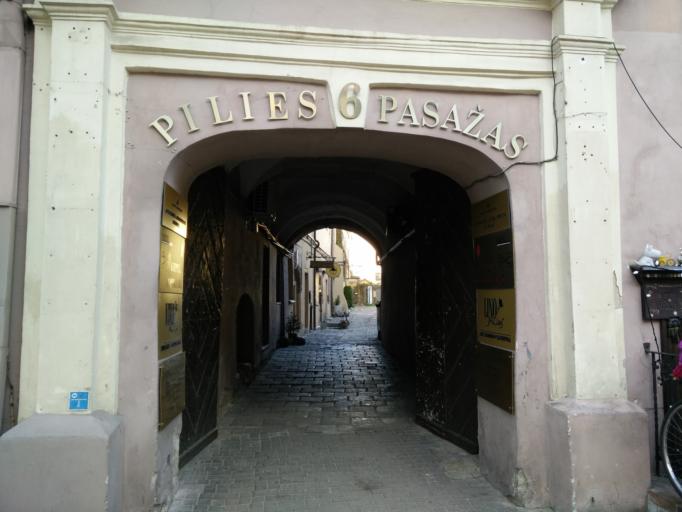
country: LT
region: Vilnius County
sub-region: Vilnius
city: Vilnius
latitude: 54.6842
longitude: 25.2896
